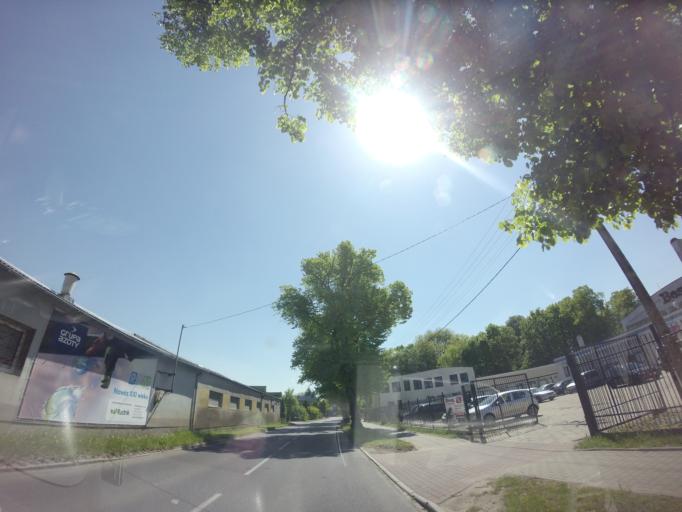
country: PL
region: West Pomeranian Voivodeship
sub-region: Powiat pyrzycki
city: Lipiany
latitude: 53.0031
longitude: 14.9766
